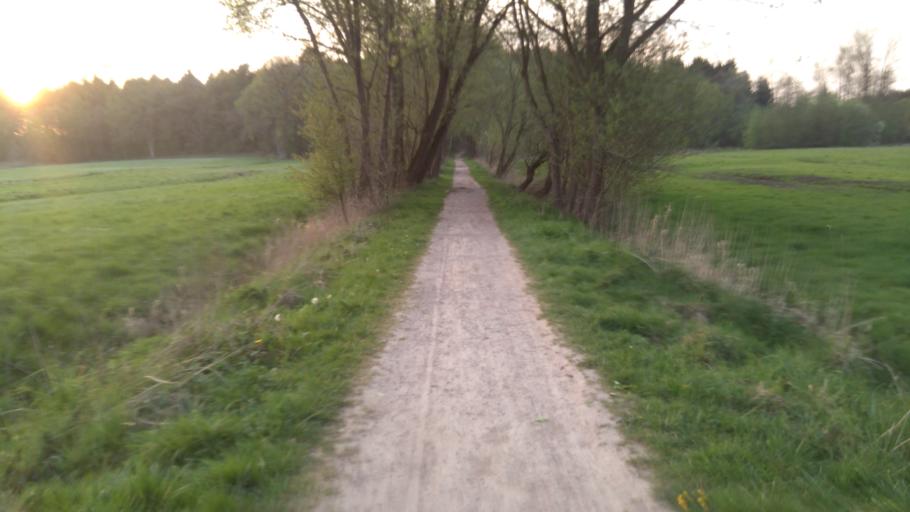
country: DE
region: Lower Saxony
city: Harsefeld
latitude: 53.4758
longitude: 9.5228
